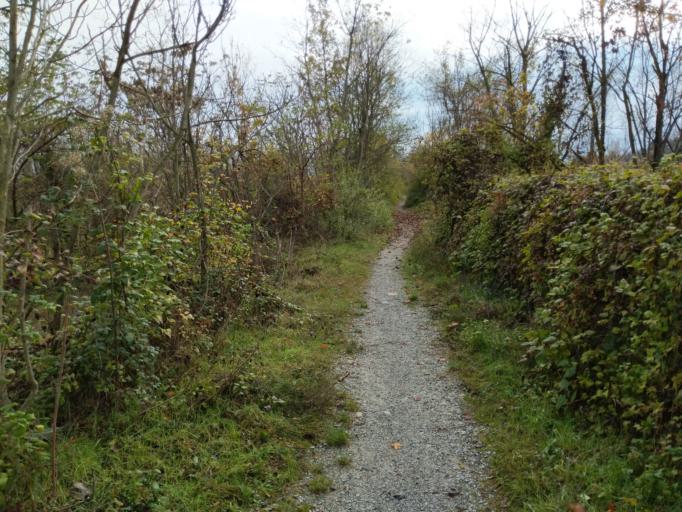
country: IT
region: Piedmont
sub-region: Provincia di Cuneo
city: Cuneo
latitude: 44.3837
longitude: 7.5526
